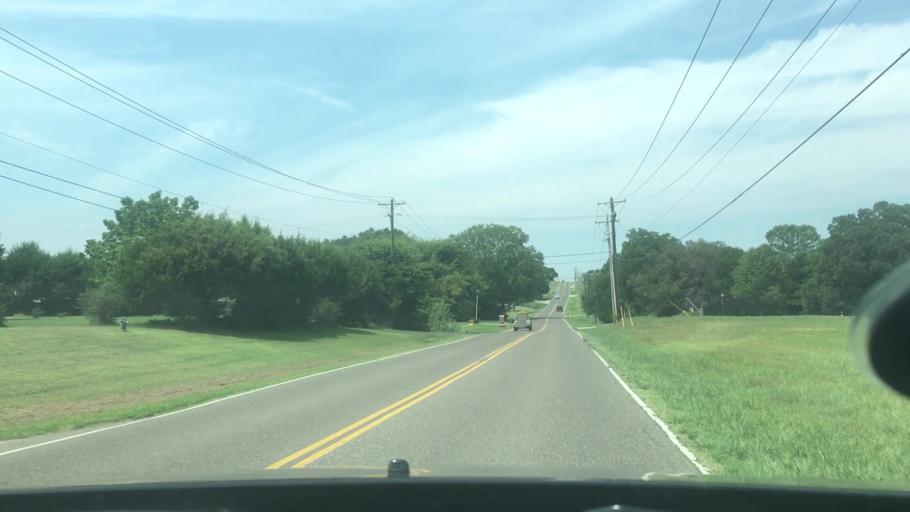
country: US
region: Oklahoma
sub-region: Pottawatomie County
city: Shawnee
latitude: 35.3617
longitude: -96.9022
